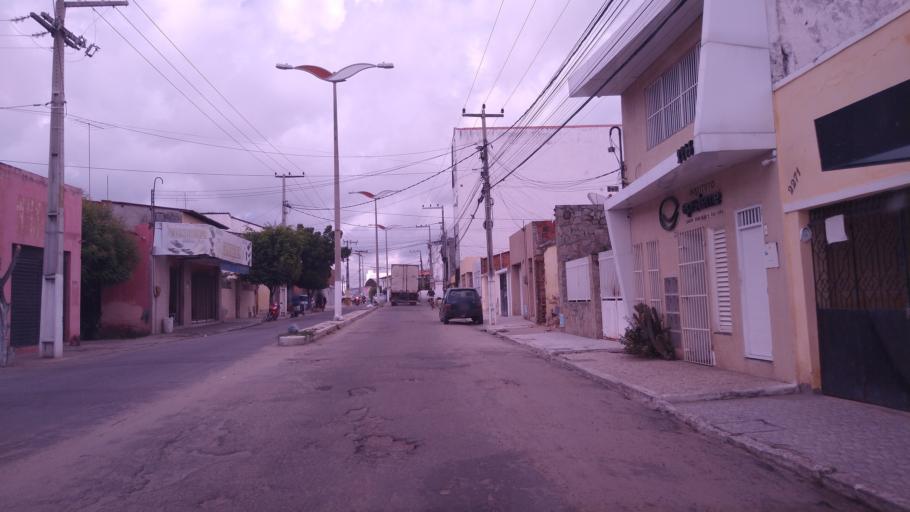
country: BR
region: Ceara
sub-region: Quixada
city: Quixada
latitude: -4.9659
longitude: -39.0160
